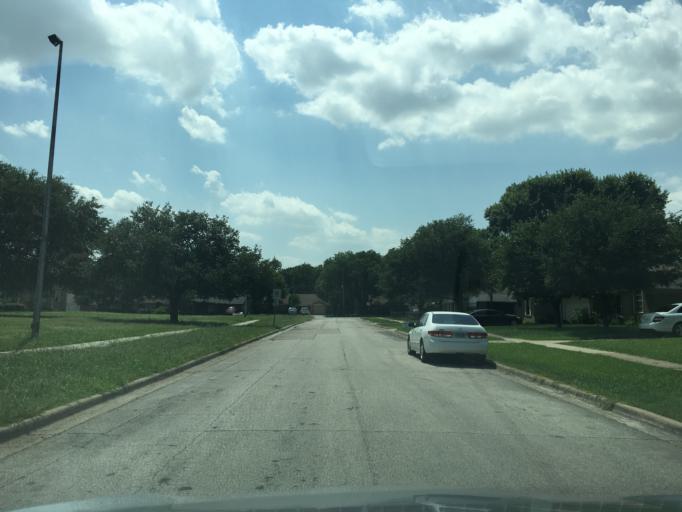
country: US
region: Texas
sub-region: Dallas County
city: Farmers Branch
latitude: 32.9192
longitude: -96.8650
